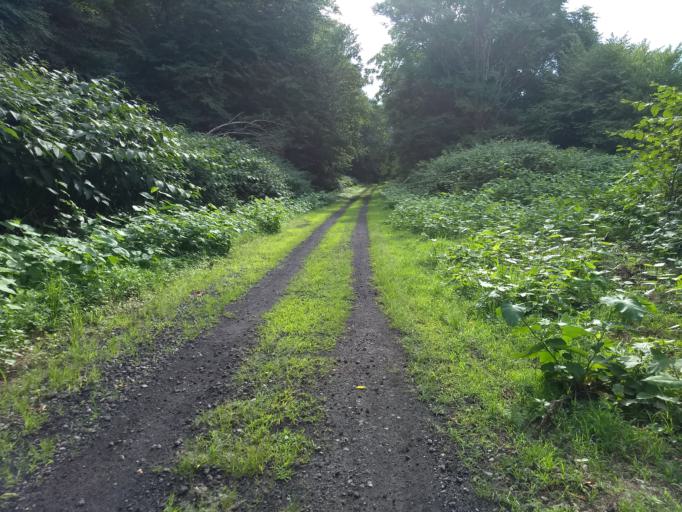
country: US
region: Pennsylvania
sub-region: Armstrong County
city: Freeport
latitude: 40.6697
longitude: -79.6795
